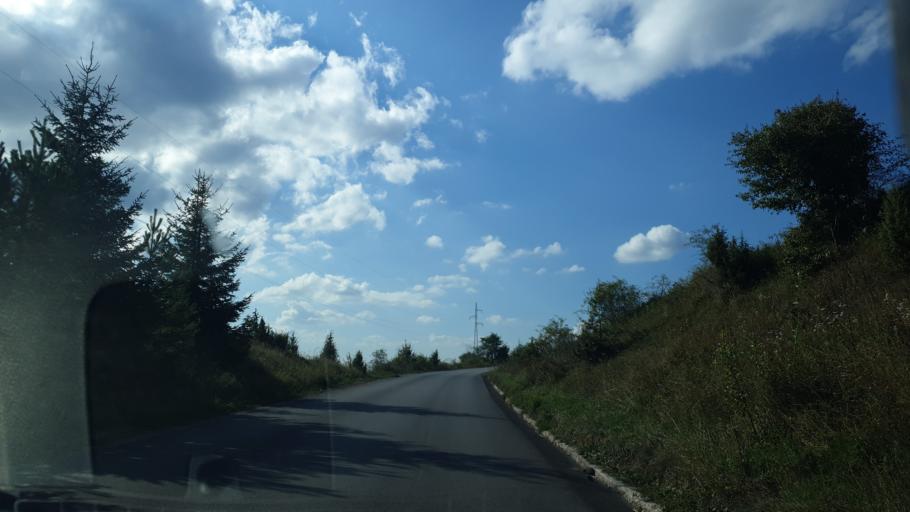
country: RS
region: Central Serbia
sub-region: Zlatiborski Okrug
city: Nova Varos
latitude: 43.4263
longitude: 19.8991
